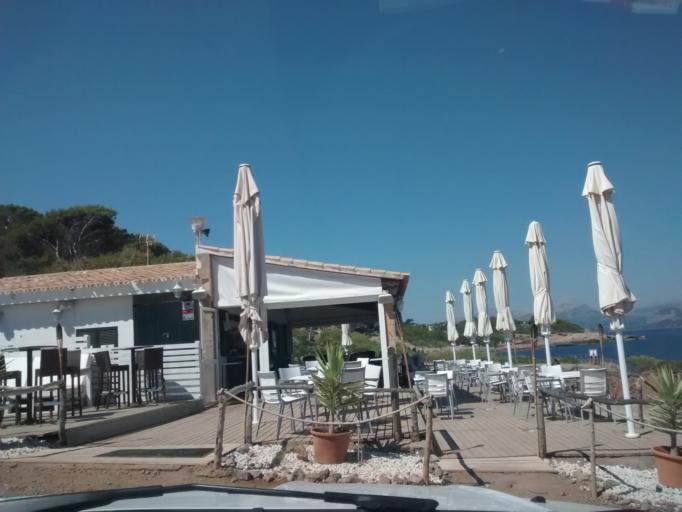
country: ES
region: Balearic Islands
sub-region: Illes Balears
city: Port d'Alcudia
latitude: 39.8726
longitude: 3.1609
